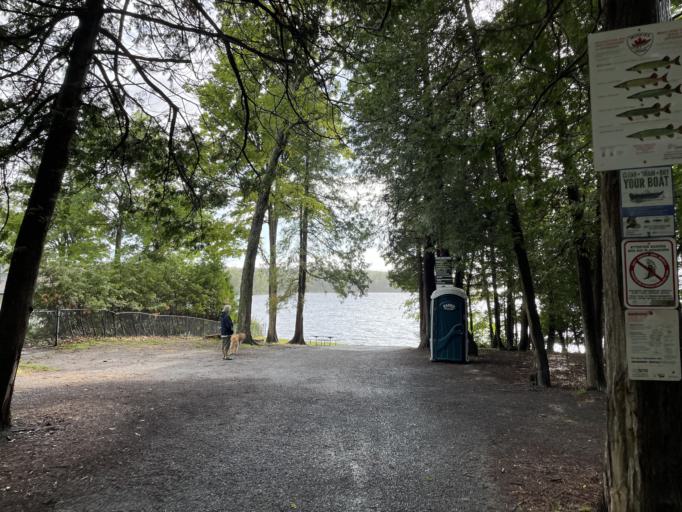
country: CA
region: Ontario
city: Quinte West
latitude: 44.4879
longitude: -77.8571
